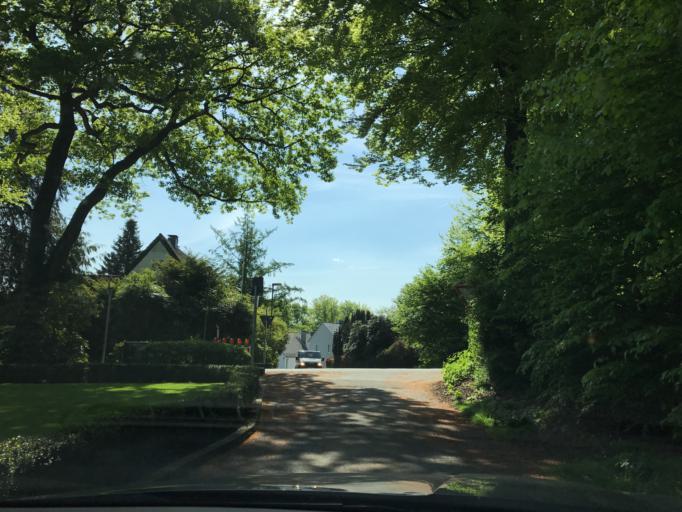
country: DE
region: North Rhine-Westphalia
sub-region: Regierungsbezirk Dusseldorf
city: Essen
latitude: 51.4163
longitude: 7.0421
